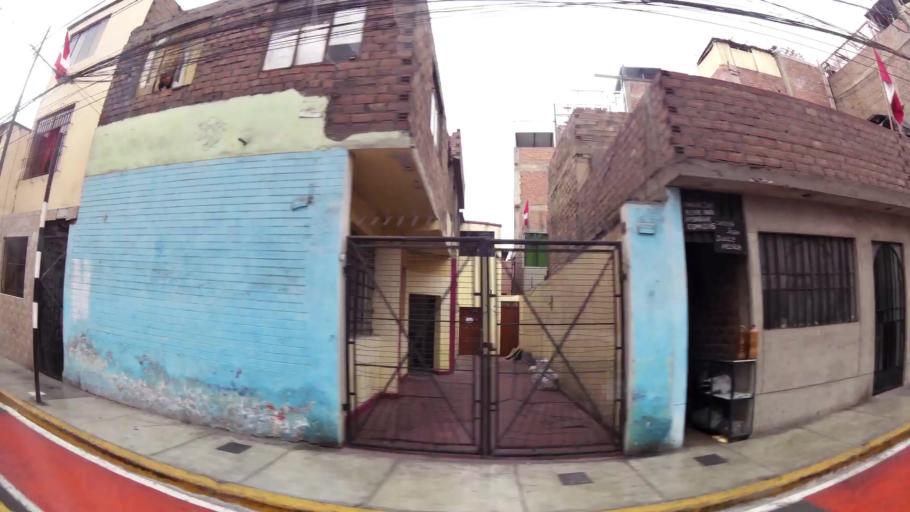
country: PE
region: Lima
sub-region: Lima
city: Surco
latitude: -12.1442
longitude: -77.0052
